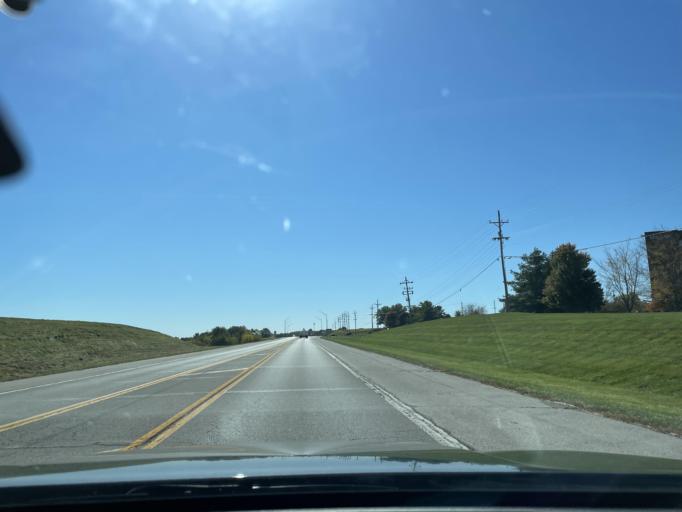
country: US
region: Missouri
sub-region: Buchanan County
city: Saint Joseph
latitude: 39.7736
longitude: -94.7680
